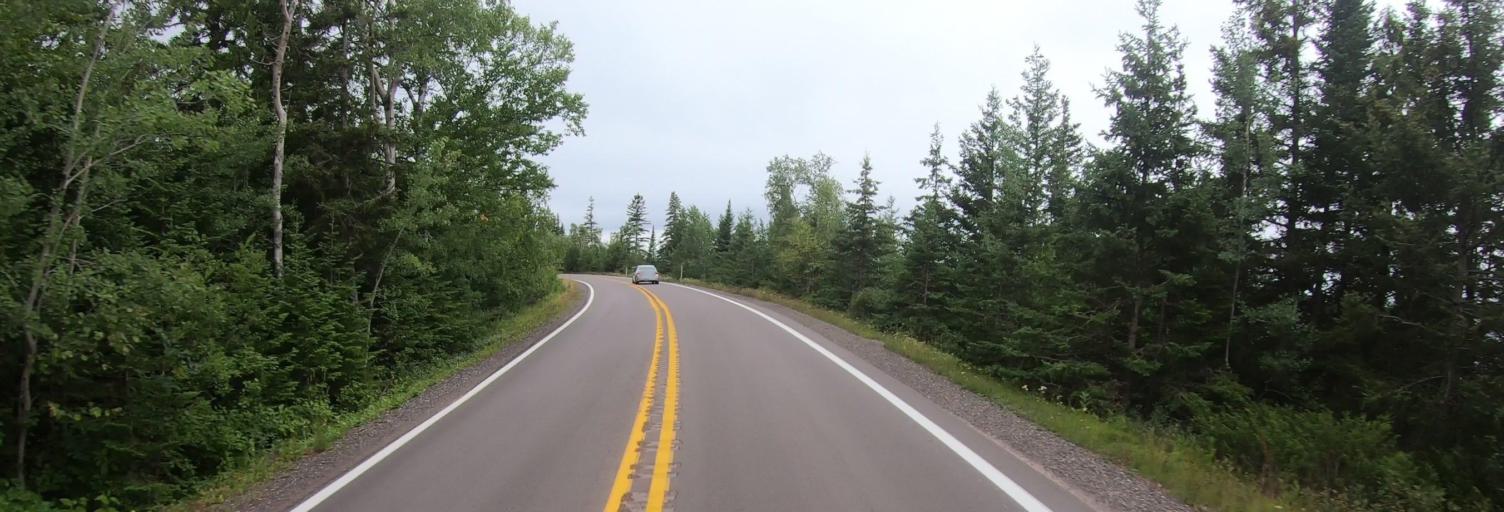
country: US
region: Michigan
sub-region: Keweenaw County
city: Eagle River
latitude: 47.4771
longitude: -88.0114
